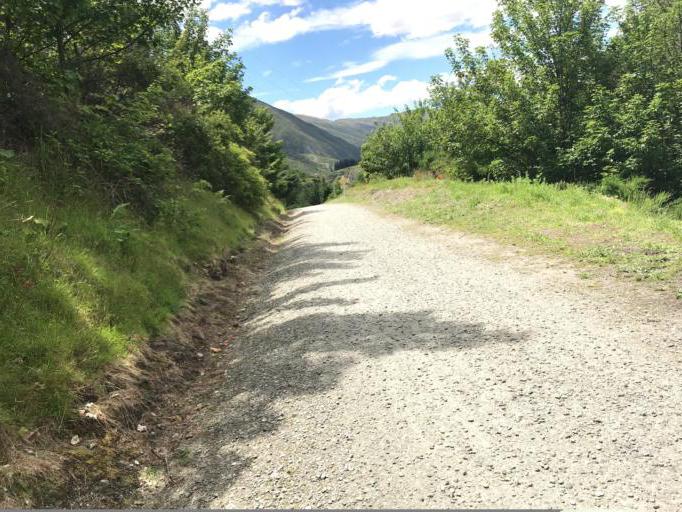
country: NZ
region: Otago
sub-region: Queenstown-Lakes District
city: Arrowtown
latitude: -45.0087
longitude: 168.8964
